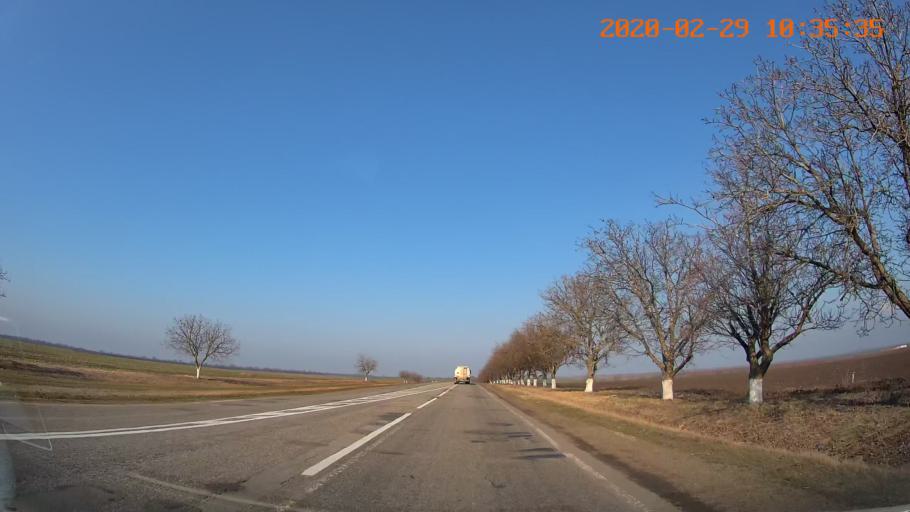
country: MD
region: Anenii Noi
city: Varnita
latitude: 46.9872
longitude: 29.5181
